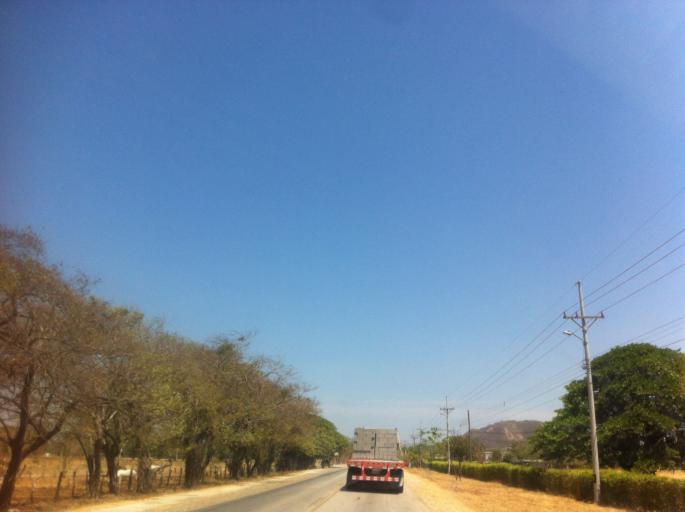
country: CR
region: Guanacaste
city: Santa Cruz
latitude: 10.2635
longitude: -85.5685
